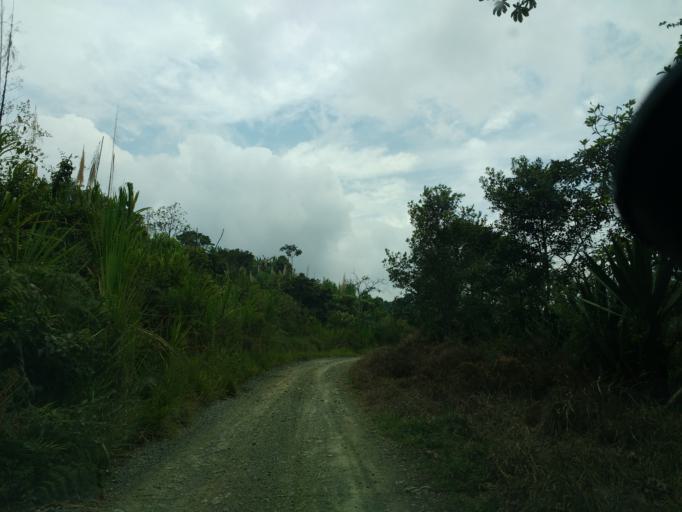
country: CO
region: Cauca
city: Santander de Quilichao
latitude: 2.9147
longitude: -76.4795
